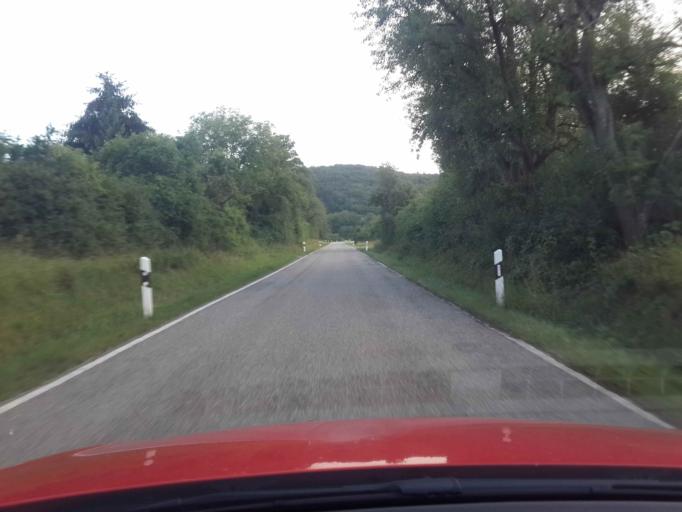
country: DE
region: Baden-Wuerttemberg
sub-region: Regierungsbezirk Stuttgart
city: Zaberfeld
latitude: 49.0488
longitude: 8.9269
